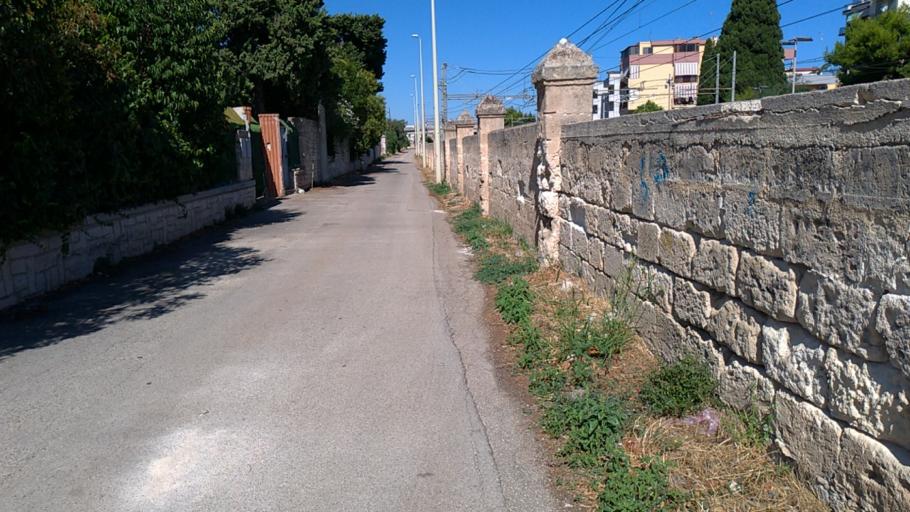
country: IT
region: Apulia
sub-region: Provincia di Bari
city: Giovinazzo
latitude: 41.1809
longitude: 16.6690
